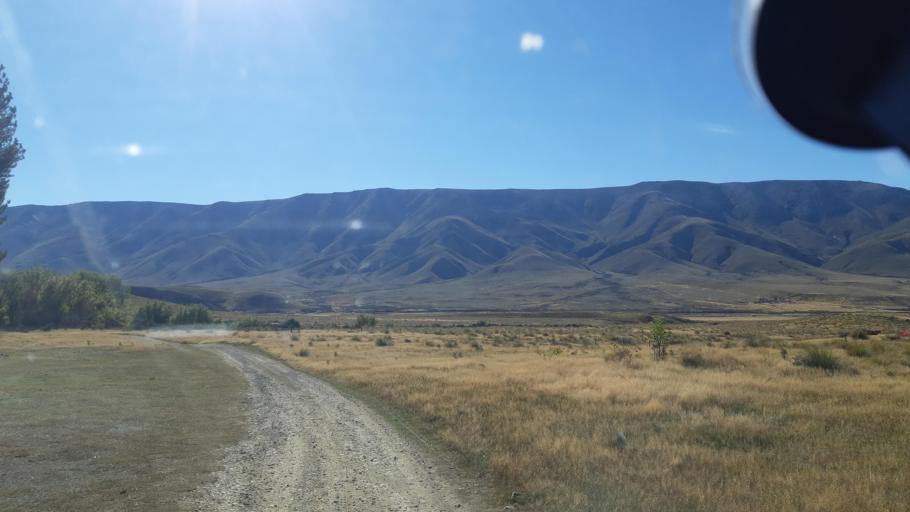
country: NZ
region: Otago
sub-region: Queenstown-Lakes District
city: Wanaka
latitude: -44.7770
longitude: 169.8894
